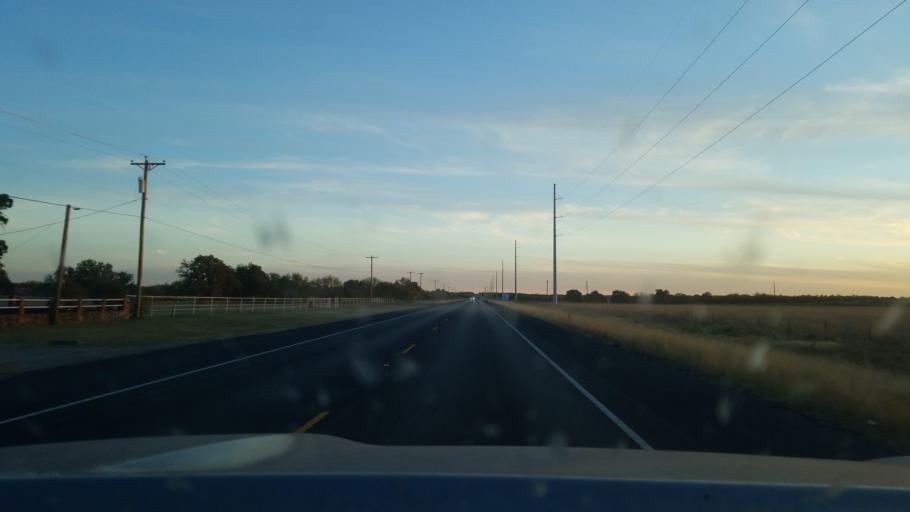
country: US
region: Texas
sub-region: Stephens County
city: Breckenridge
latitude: 32.7172
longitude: -98.9028
